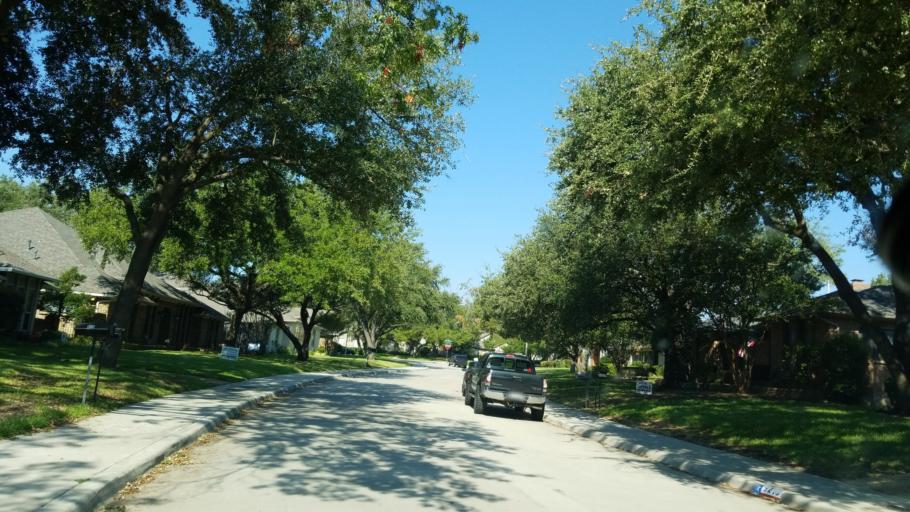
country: US
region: Texas
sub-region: Dallas County
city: Richardson
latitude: 32.9044
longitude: -96.7402
